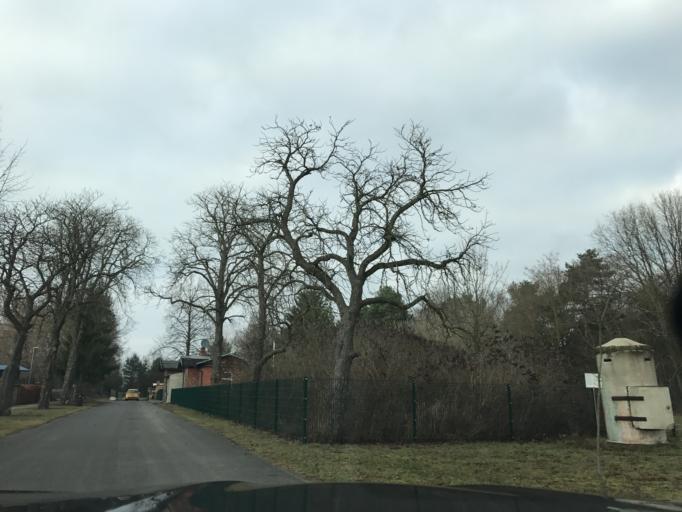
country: DE
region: Brandenburg
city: Brandenburg an der Havel
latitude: 52.3369
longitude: 12.5508
